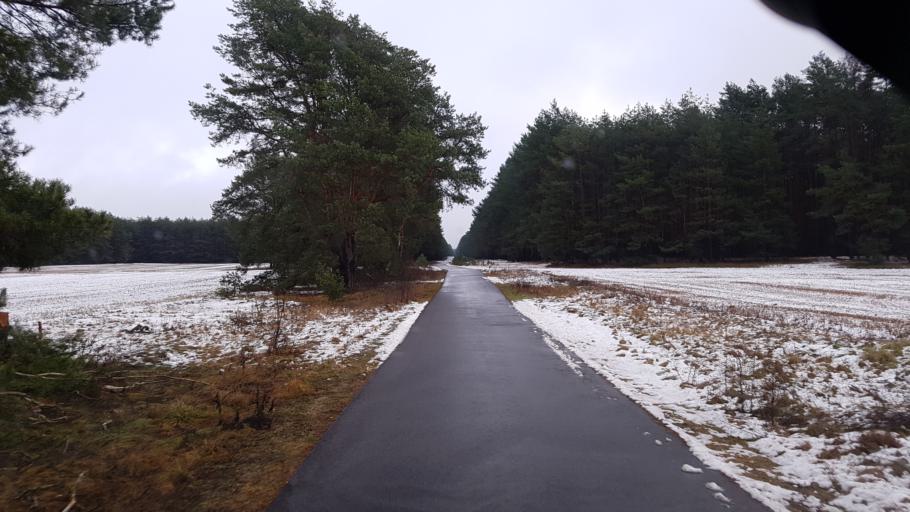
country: DE
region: Brandenburg
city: Straupitz
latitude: 51.9628
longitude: 14.1461
